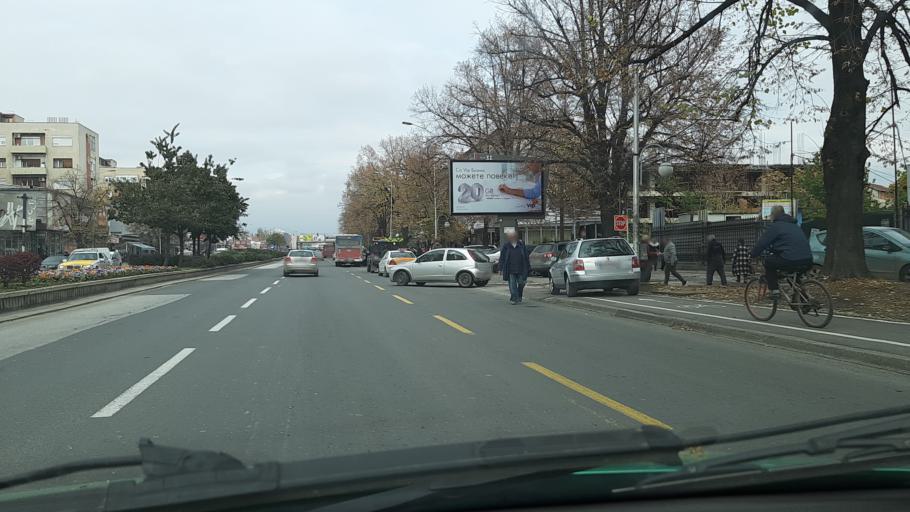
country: MK
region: Karpos
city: Skopje
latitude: 41.9995
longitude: 21.4404
